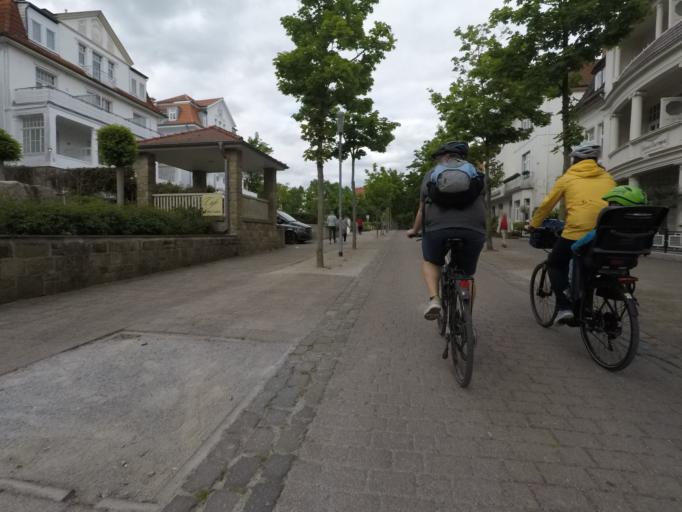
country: DE
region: North Rhine-Westphalia
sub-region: Regierungsbezirk Detmold
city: Bad Salzuflen
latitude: 52.0889
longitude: 8.7493
